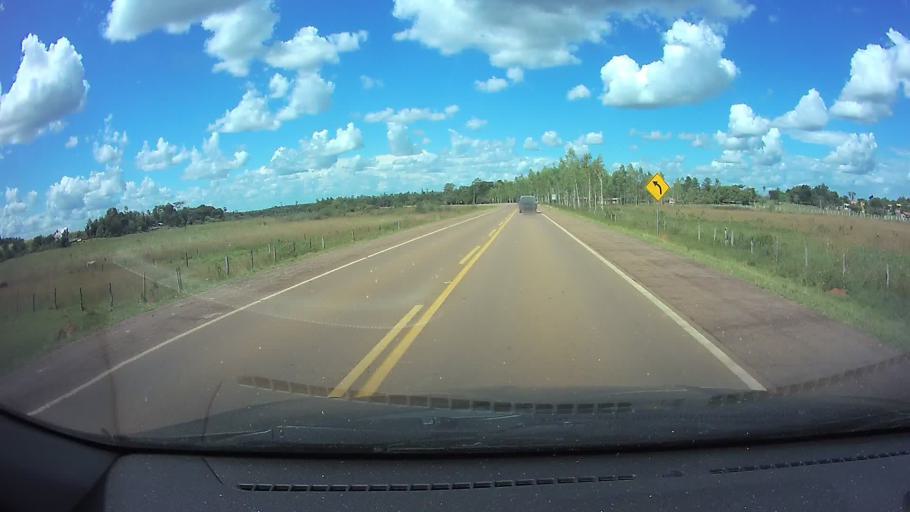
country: PY
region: Guaira
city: Itape
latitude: -25.9140
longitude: -56.6804
